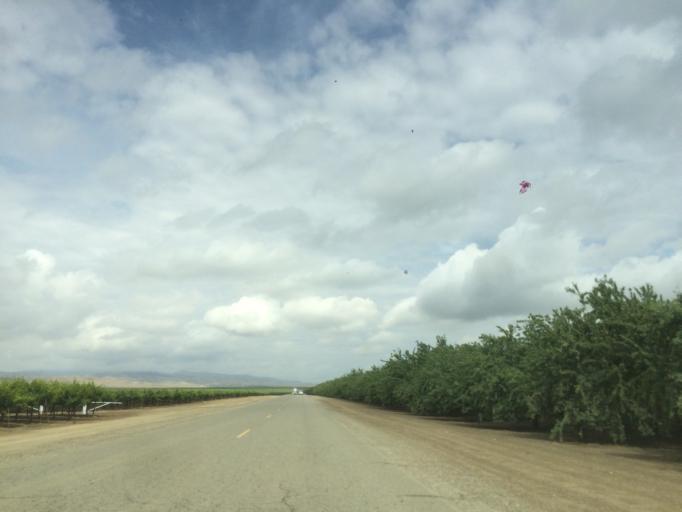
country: US
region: California
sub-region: Fresno County
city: Coalinga
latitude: 36.3785
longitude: -120.3481
